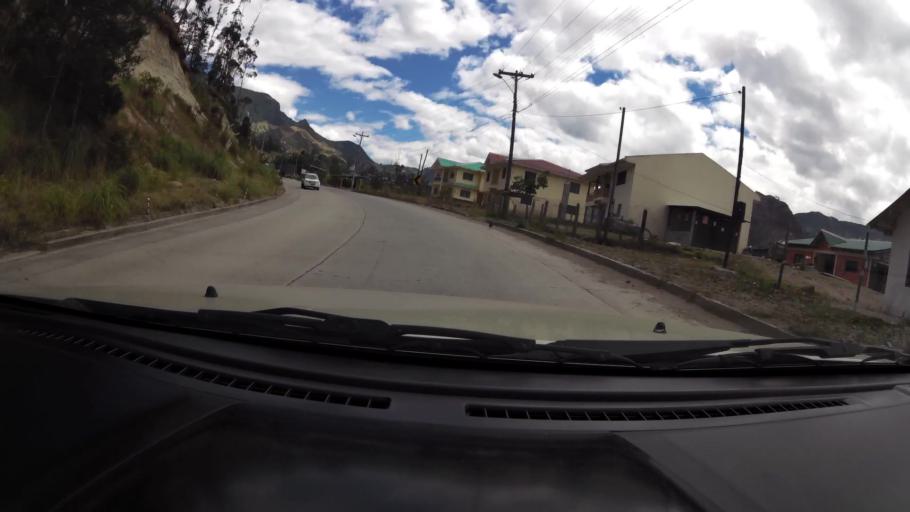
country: EC
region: Azuay
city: Cuenca
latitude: -3.1438
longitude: -79.1412
